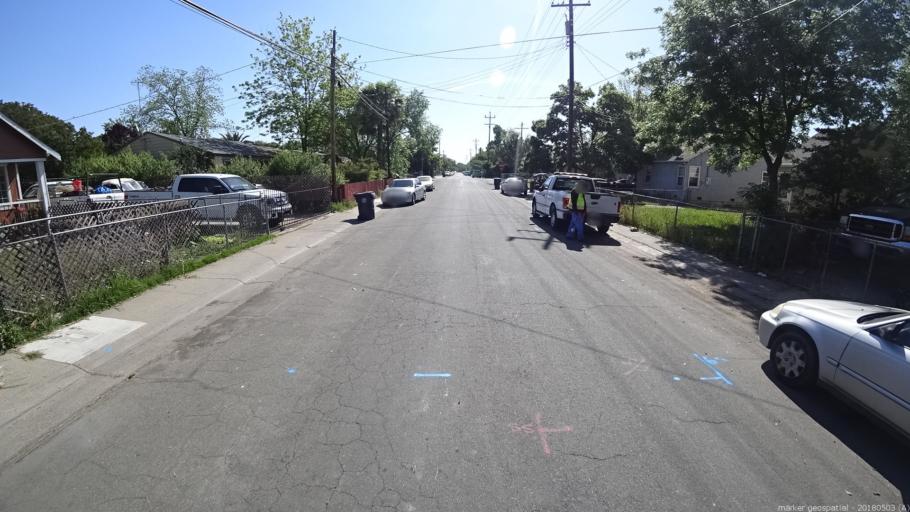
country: US
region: California
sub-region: Sacramento County
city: Sacramento
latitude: 38.6203
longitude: -121.4447
